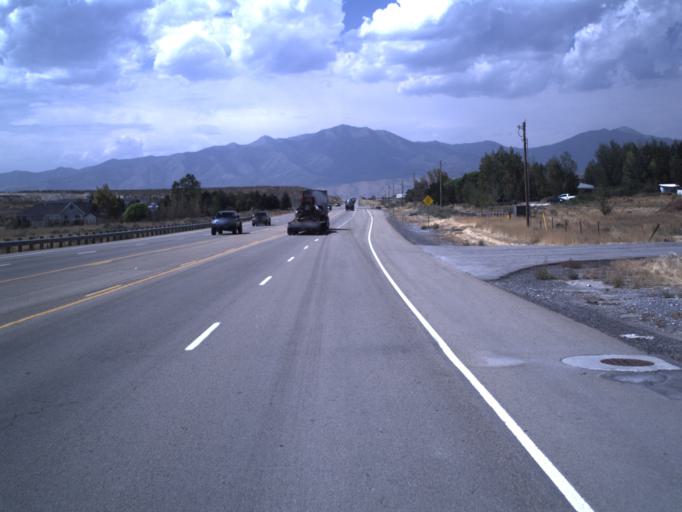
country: US
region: Utah
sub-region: Utah County
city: Eagle Mountain
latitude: 40.3804
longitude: -111.9773
